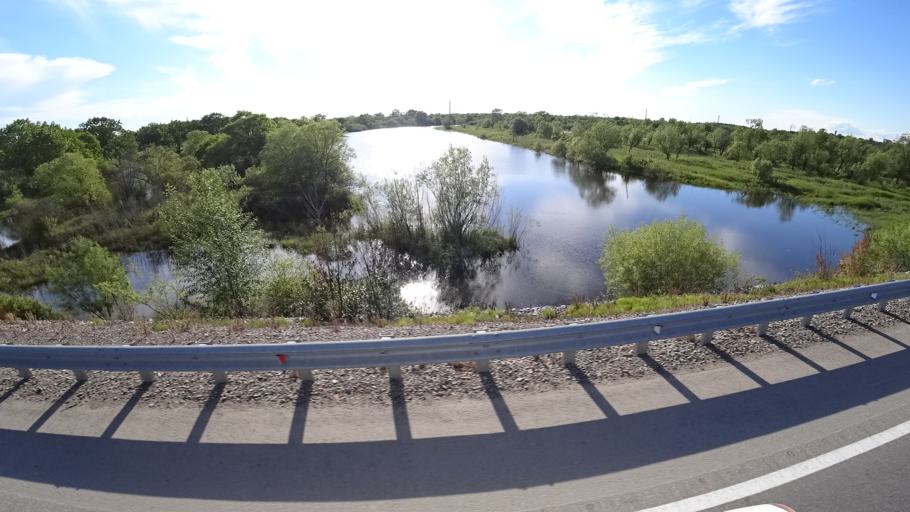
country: RU
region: Khabarovsk Krai
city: Khor
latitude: 47.8597
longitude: 134.9628
